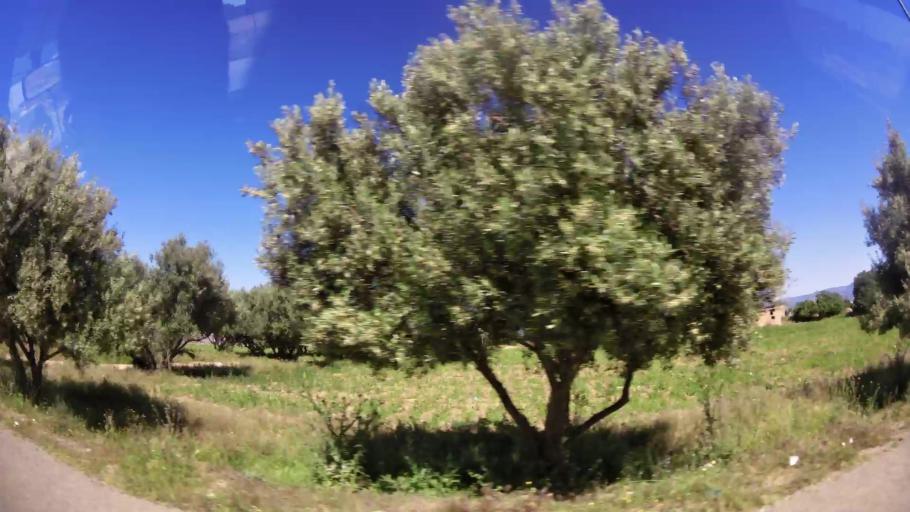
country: MA
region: Oriental
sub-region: Oujda-Angad
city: Oujda
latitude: 34.7008
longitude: -1.8566
